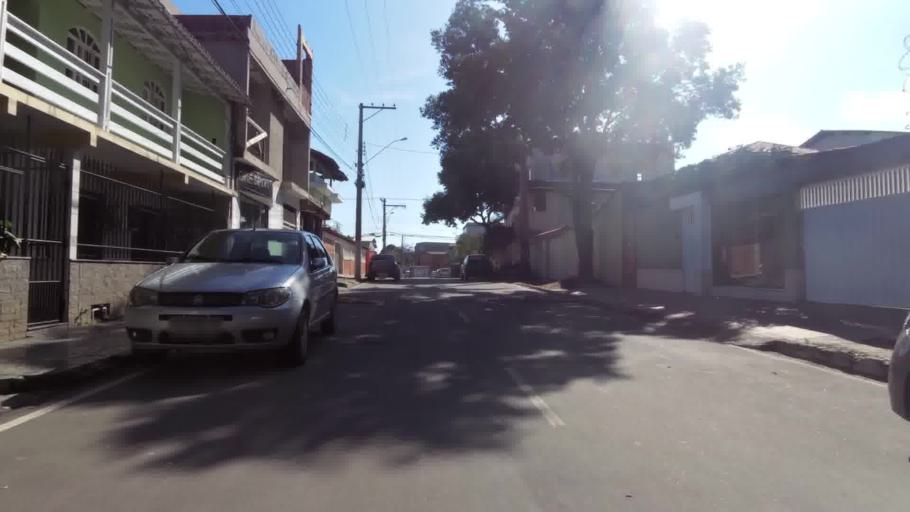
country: BR
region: Espirito Santo
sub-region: Piuma
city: Piuma
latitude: -20.8077
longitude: -40.6436
